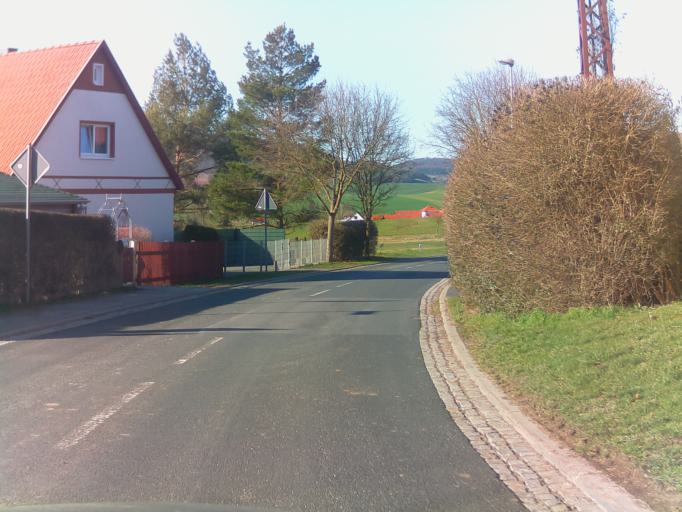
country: DE
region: Thuringia
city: Henneberg
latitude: 50.5055
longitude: 10.3201
